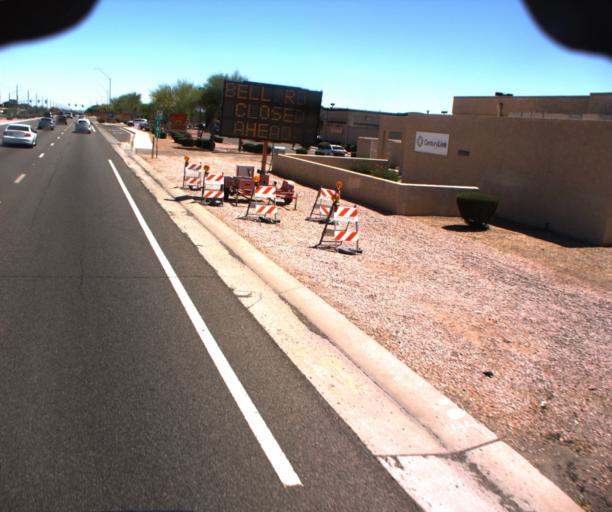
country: US
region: Arizona
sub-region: Maricopa County
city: Sun City West
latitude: 33.6562
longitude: -112.3730
